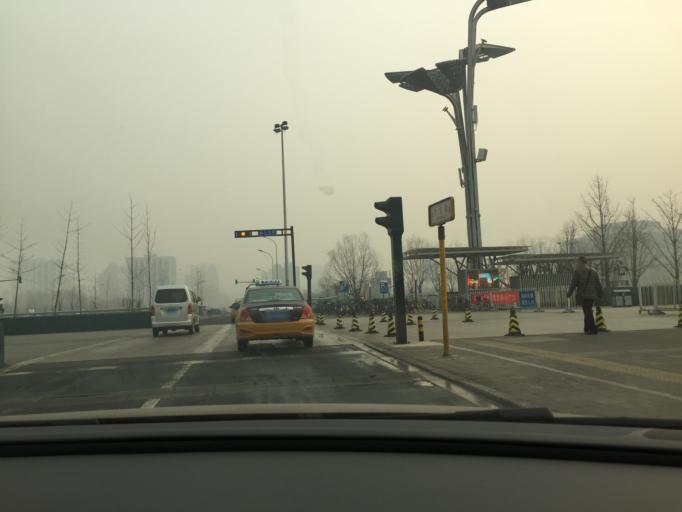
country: CN
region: Beijing
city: Datun
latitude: 40.0006
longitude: 116.3865
